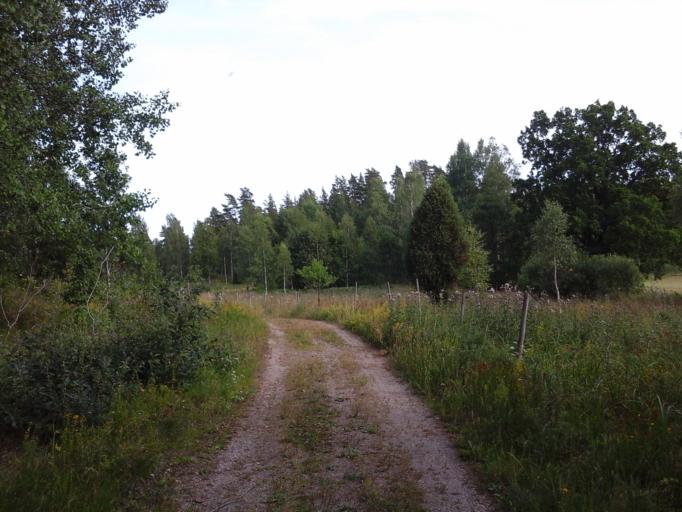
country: SE
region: Soedermanland
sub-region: Eskilstuna Kommun
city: Arla
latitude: 59.2463
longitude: 16.7697
